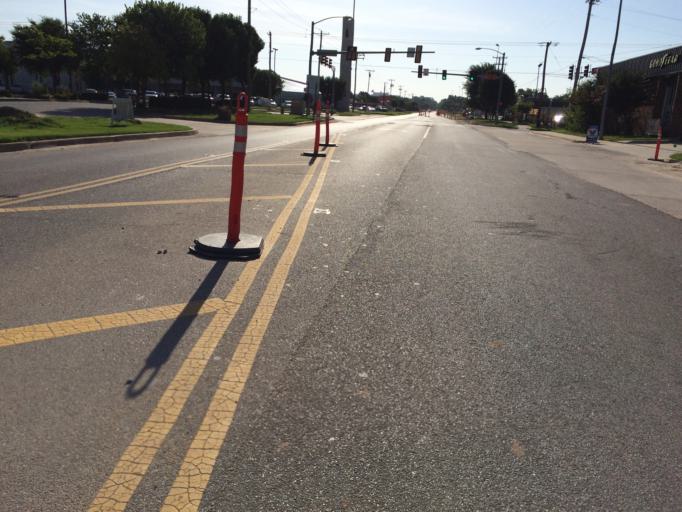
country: US
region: Oklahoma
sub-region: Cleveland County
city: Norman
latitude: 35.2039
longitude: -97.4687
